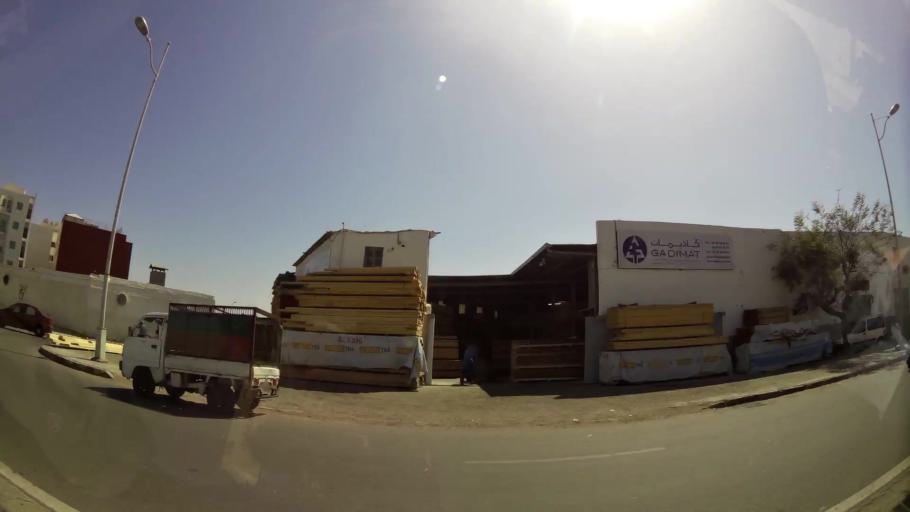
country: MA
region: Oued ed Dahab-Lagouira
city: Dakhla
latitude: 30.4173
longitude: -9.5747
